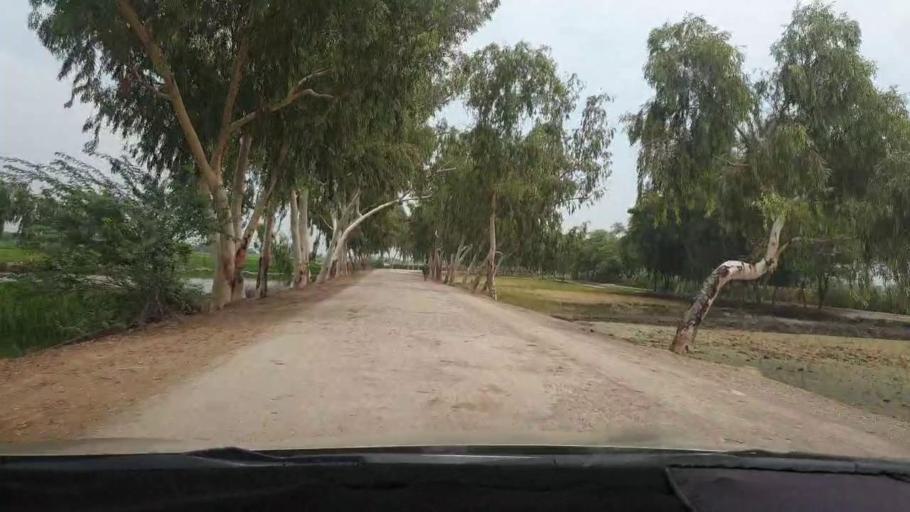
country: PK
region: Sindh
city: Ratodero
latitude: 27.7647
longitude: 68.3248
